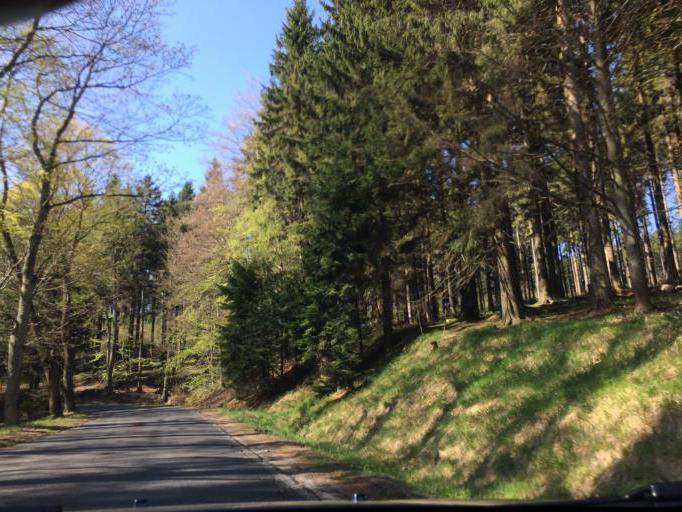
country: PL
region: Lower Silesian Voivodeship
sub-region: Powiat klodzki
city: Jugow
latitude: 50.6603
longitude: 16.5213
